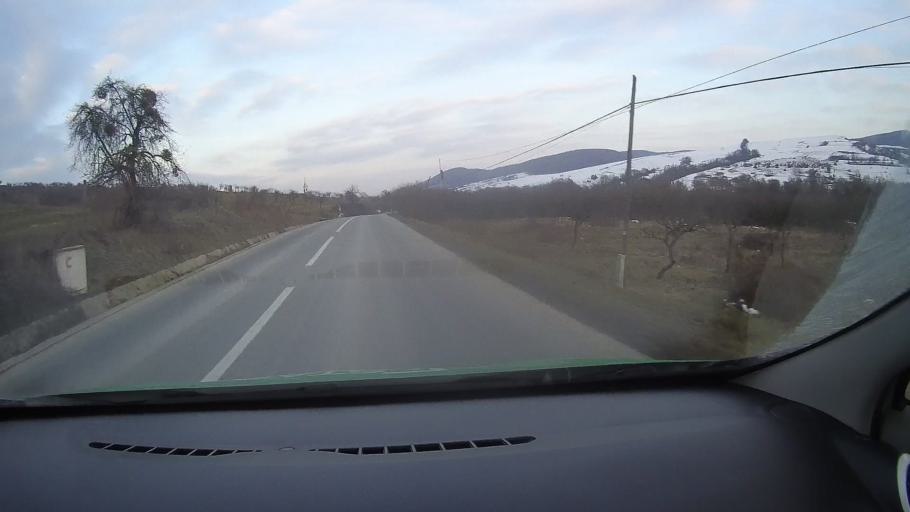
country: RO
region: Harghita
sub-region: Comuna Lupeni
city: Lupeni
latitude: 46.3574
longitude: 25.1601
